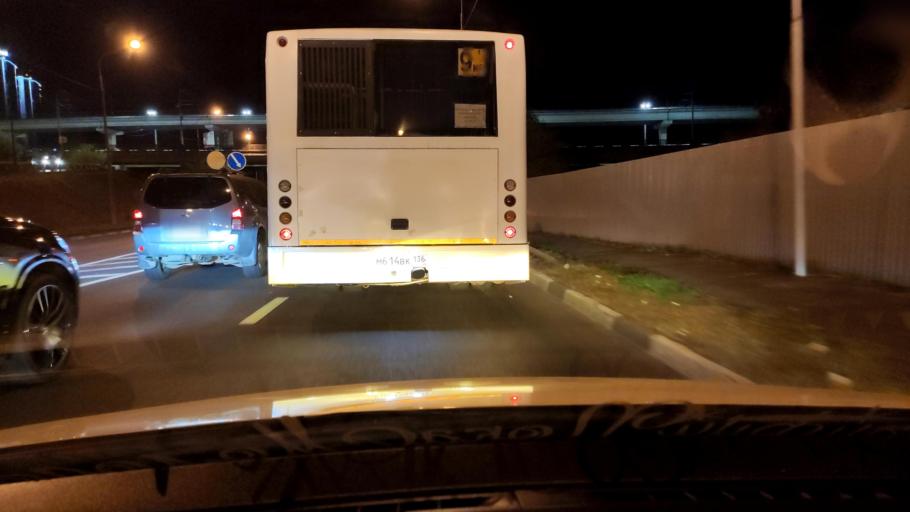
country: RU
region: Voronezj
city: Voronezh
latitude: 51.6921
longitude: 39.2332
